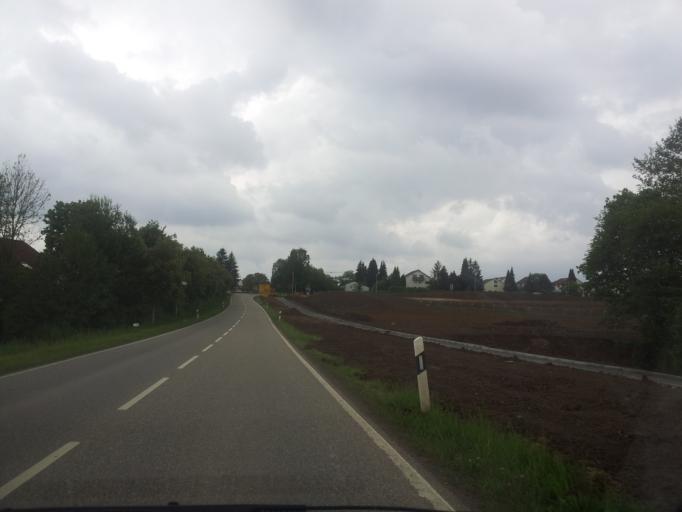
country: DE
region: Baden-Wuerttemberg
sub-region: Regierungsbezirk Stuttgart
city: Abstatt
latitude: 49.0716
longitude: 9.2960
